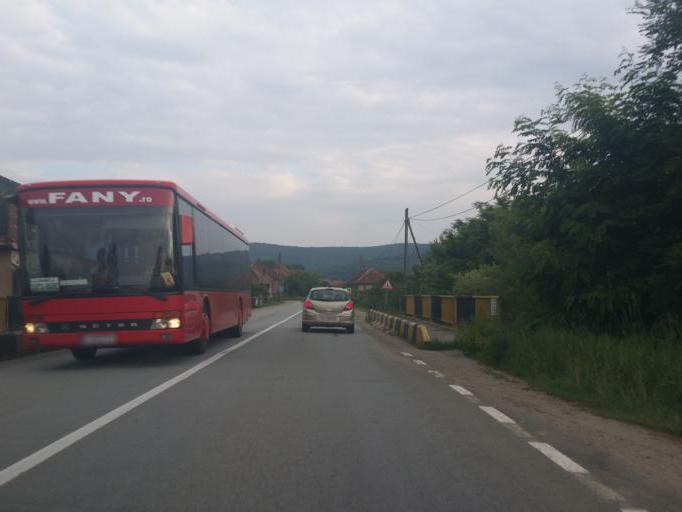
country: RO
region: Salaj
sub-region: Comuna Zimbor
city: Zimbor
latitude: 46.9891
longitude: 23.2516
